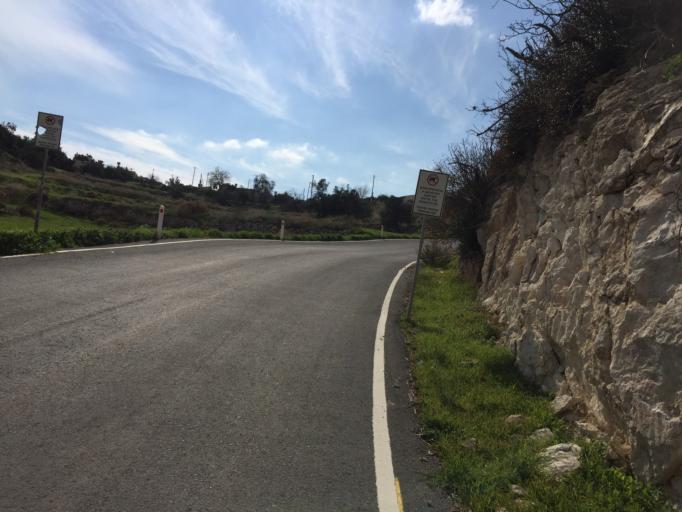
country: CY
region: Larnaka
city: Agios Tychon
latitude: 34.7461
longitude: 33.1317
